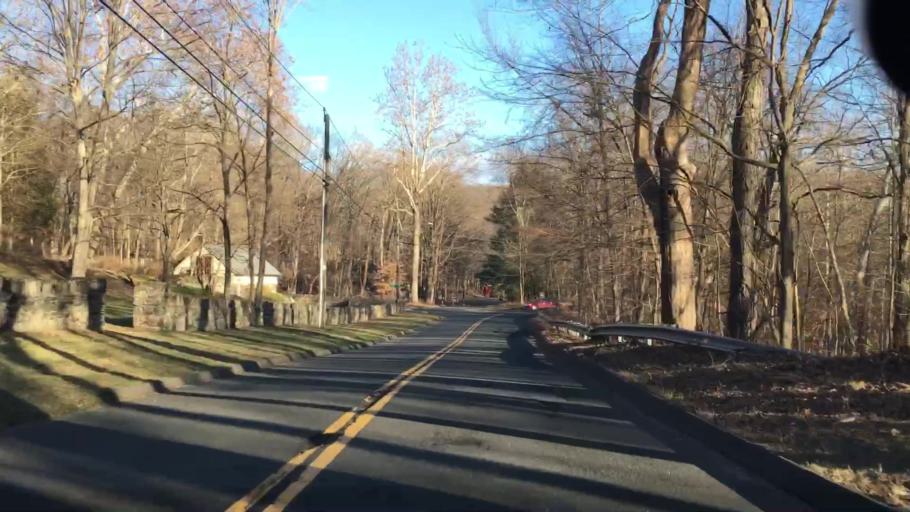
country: US
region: Connecticut
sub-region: Fairfield County
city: Newtown
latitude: 41.4608
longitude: -73.3284
